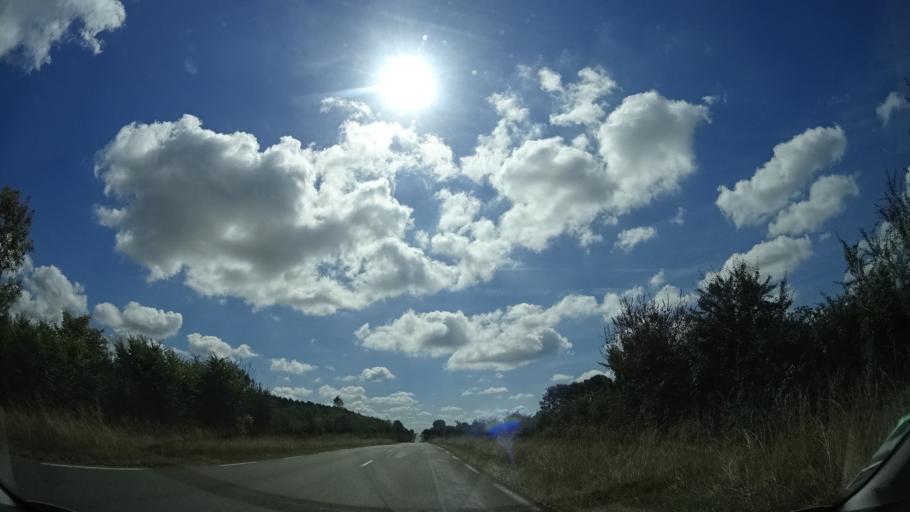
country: FR
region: Pays de la Loire
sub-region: Departement de la Mayenne
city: Meslay-du-Maine
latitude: 47.9329
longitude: -0.5008
